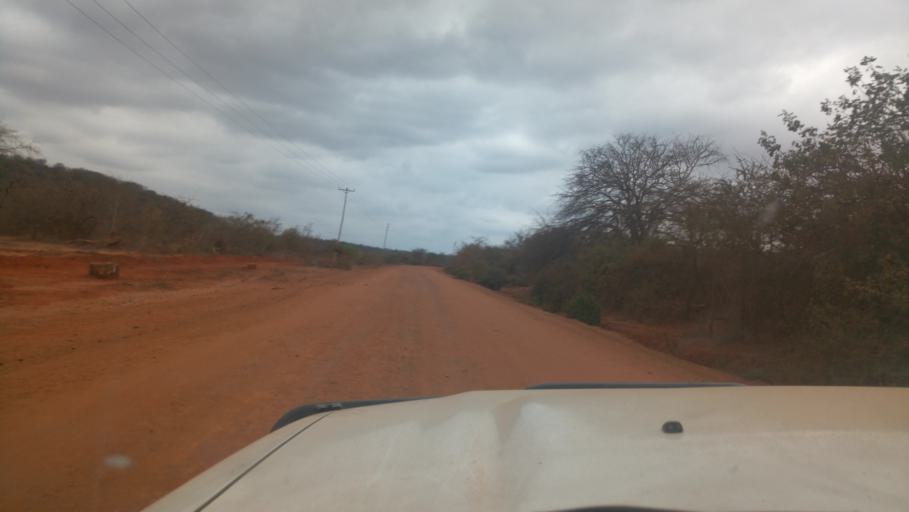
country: KE
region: Makueni
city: Wote
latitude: -1.8876
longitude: 37.9806
